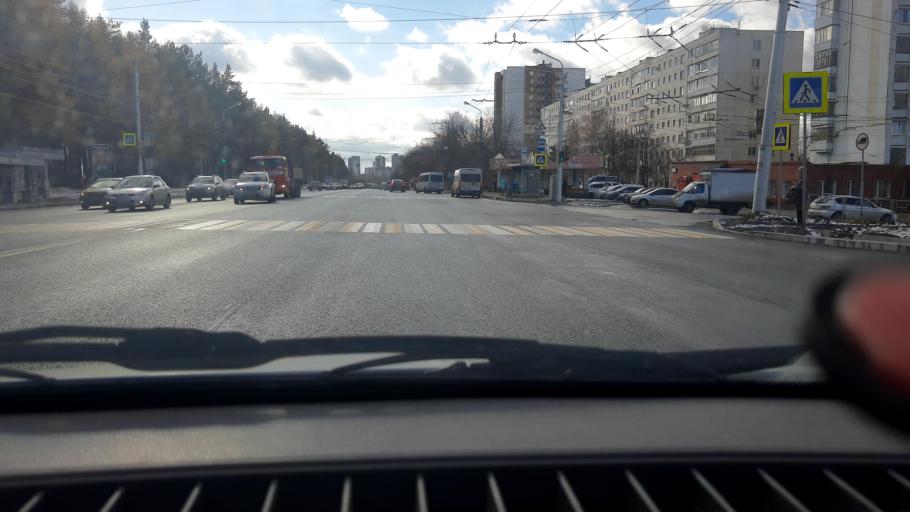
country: RU
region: Bashkortostan
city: Ufa
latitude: 54.7405
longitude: 56.0282
